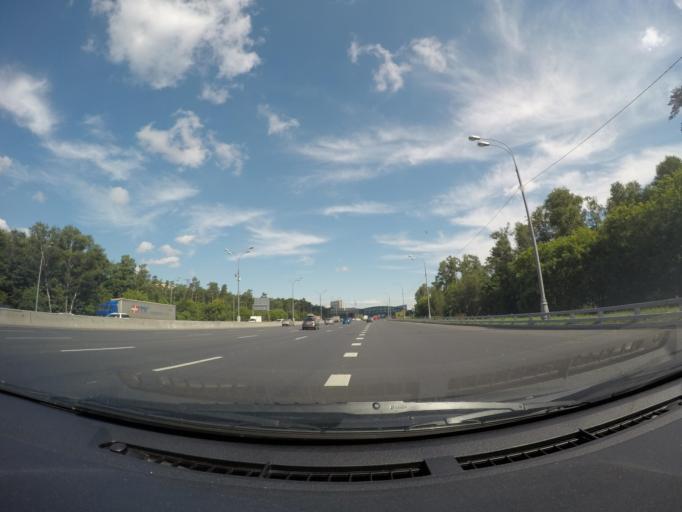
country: RU
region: Moscow
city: Vykhino-Zhulebino
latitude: 55.6918
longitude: 37.8297
